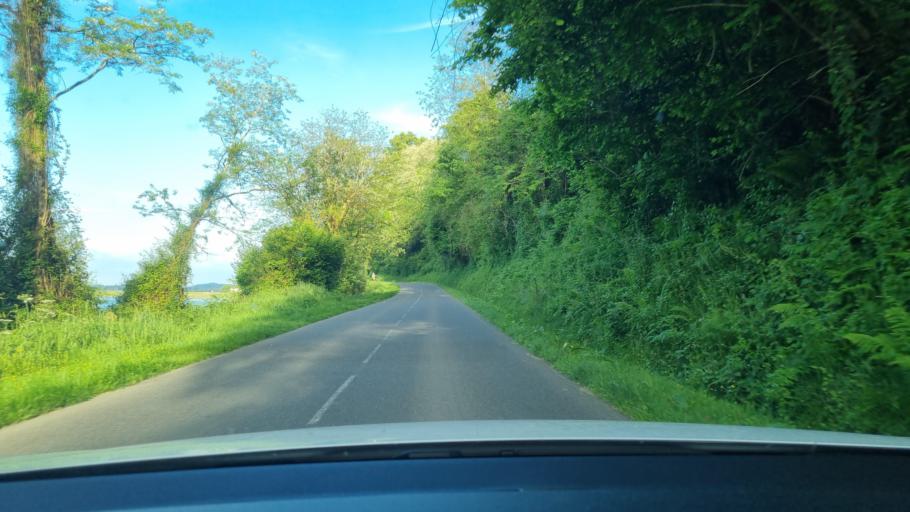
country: FR
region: Aquitaine
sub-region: Departement des Landes
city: Peyrehorade
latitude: 43.5362
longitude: -1.1551
